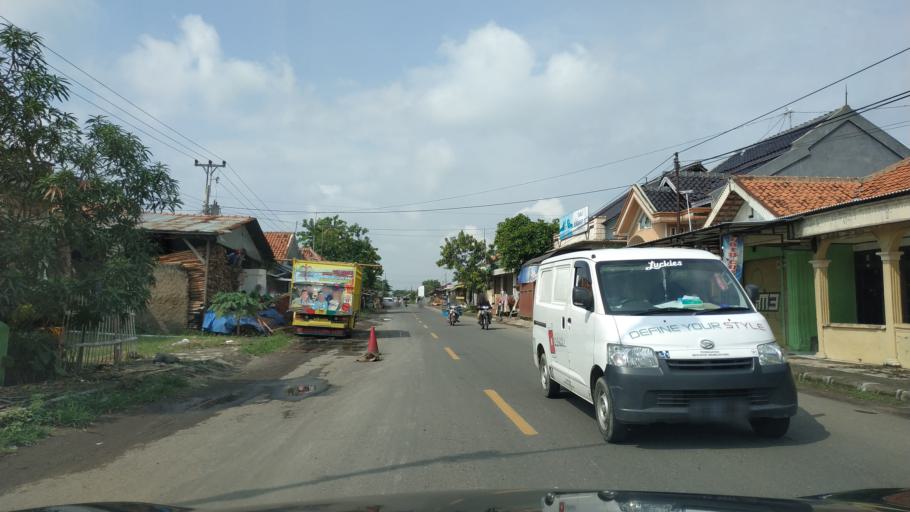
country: ID
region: Central Java
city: Ketanggungan
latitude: -6.8816
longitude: 108.8854
